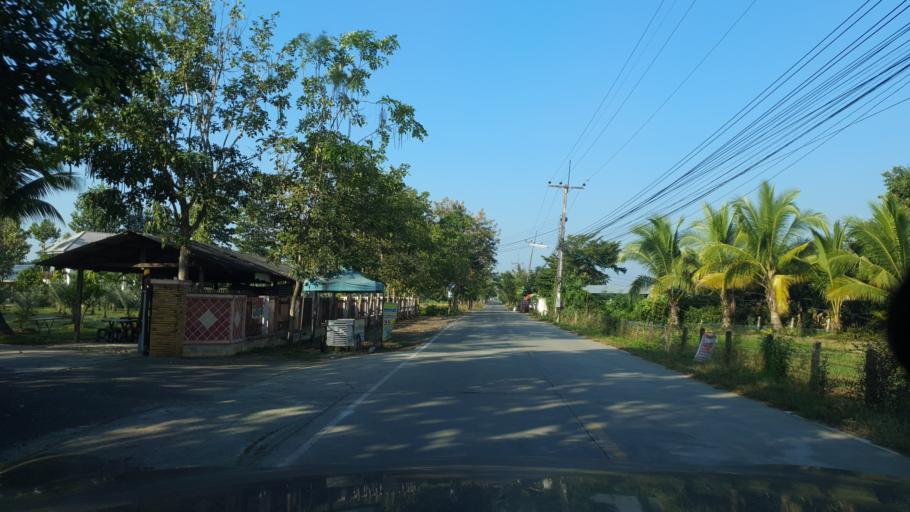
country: TH
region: Chiang Mai
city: San Kamphaeng
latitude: 18.7215
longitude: 99.0858
